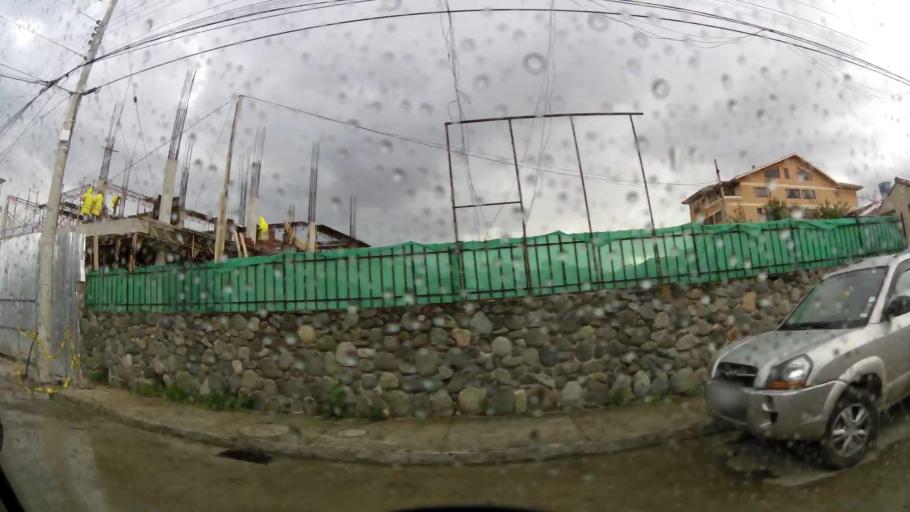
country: EC
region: Azuay
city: Cuenca
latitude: -2.8919
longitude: -79.0230
